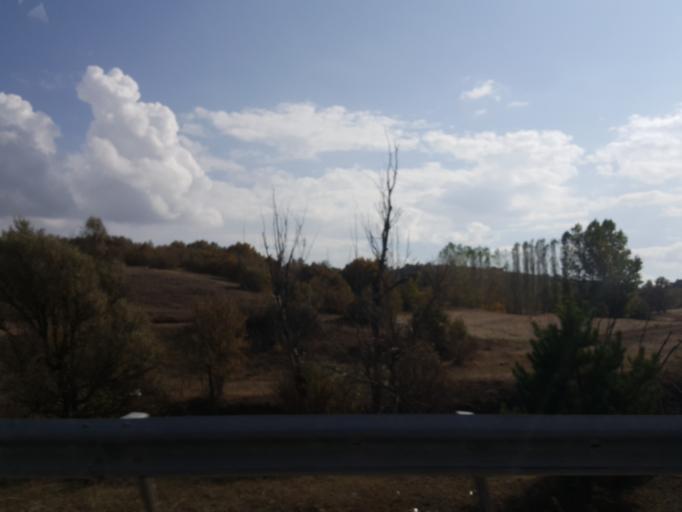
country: TR
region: Corum
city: Alaca
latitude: 40.3181
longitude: 34.6866
